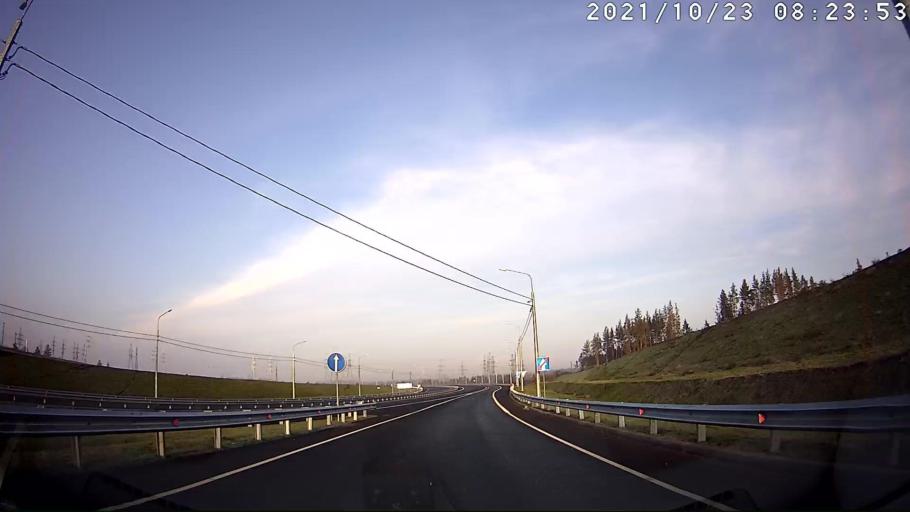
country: RU
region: Saratov
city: Sennoy
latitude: 52.1429
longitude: 46.9159
